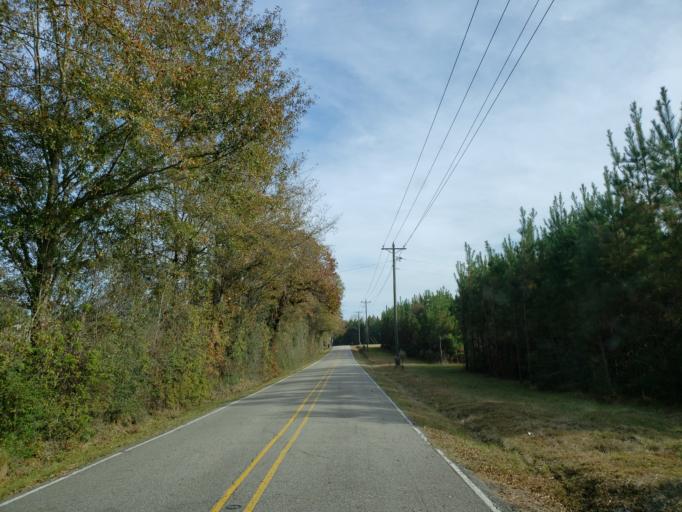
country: US
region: Mississippi
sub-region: Forrest County
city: Rawls Springs
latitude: 31.4156
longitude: -89.4181
